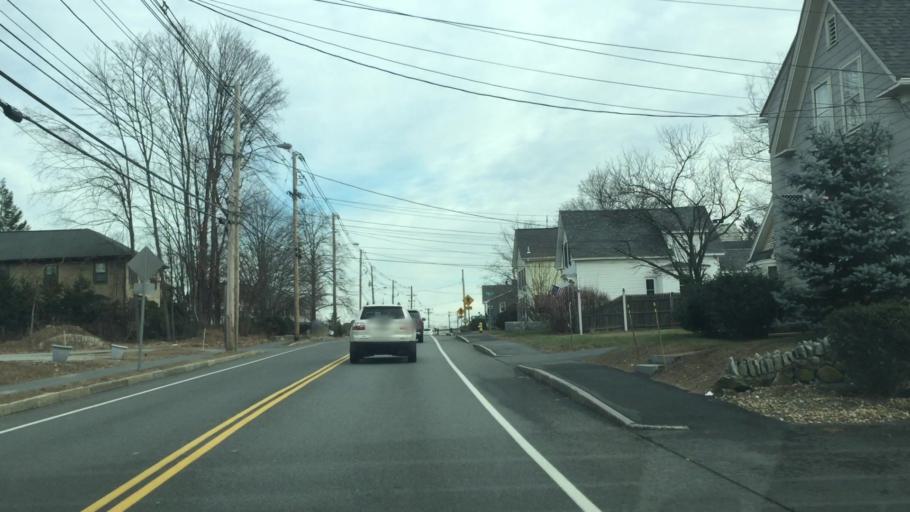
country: US
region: New Hampshire
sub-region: Rockingham County
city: Salem
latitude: 42.7824
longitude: -71.2353
